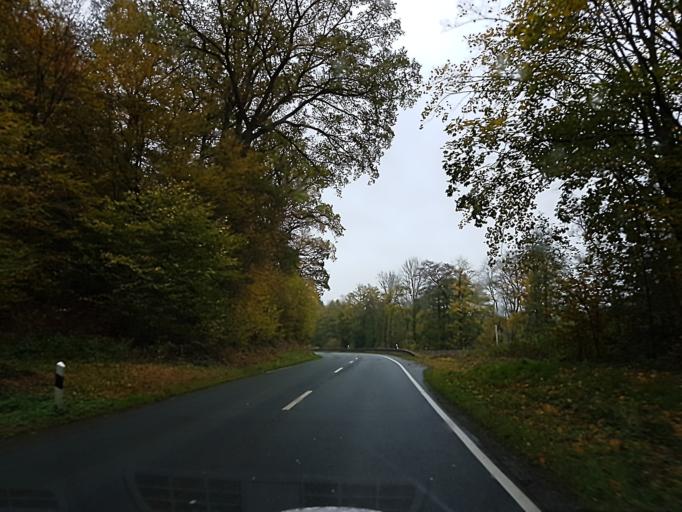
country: DE
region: North Rhine-Westphalia
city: Kierspe
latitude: 51.1869
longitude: 7.5716
